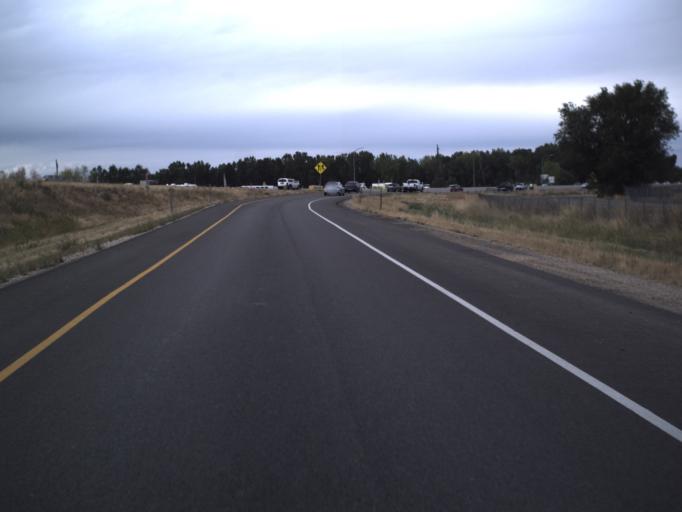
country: US
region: Utah
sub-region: Weber County
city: Marriott-Slaterville
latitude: 41.2300
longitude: -112.0114
